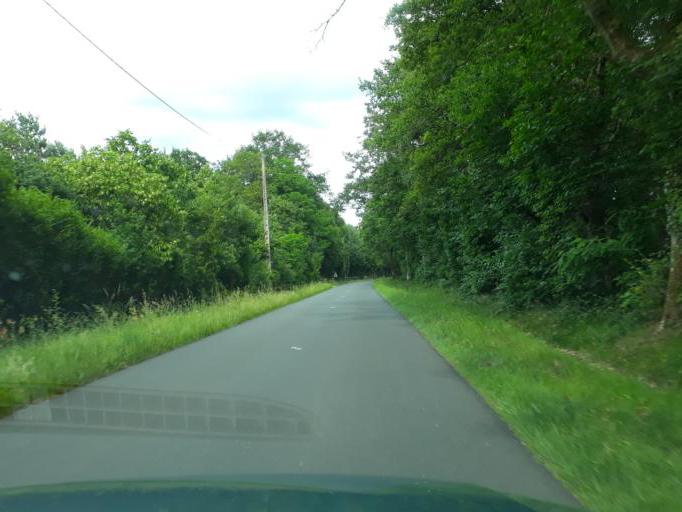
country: FR
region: Centre
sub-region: Departement du Loiret
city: Menestreau-en-Villette
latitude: 47.7185
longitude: 2.0077
